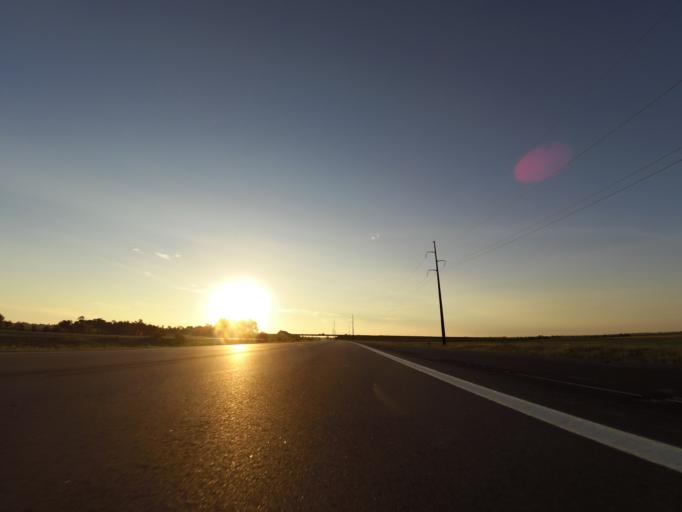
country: US
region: Kansas
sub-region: Reno County
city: South Hutchinson
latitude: 38.0131
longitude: -97.9747
